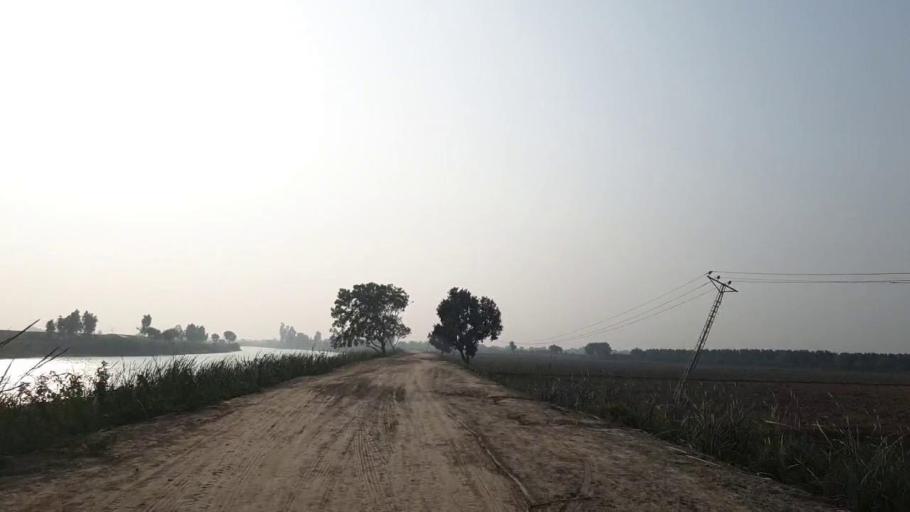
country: PK
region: Sindh
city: Tando Muhammad Khan
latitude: 25.0958
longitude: 68.5771
